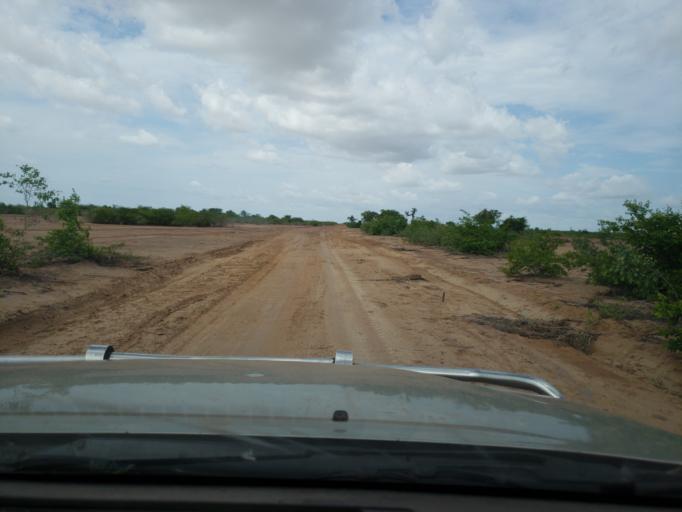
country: ML
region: Segou
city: Bla
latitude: 12.7079
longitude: -5.7032
